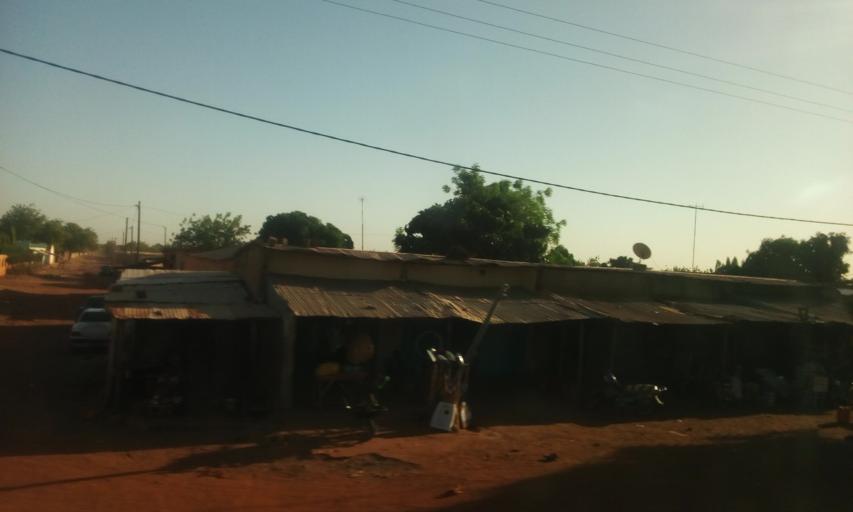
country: ML
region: Segou
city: Baroueli
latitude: 12.7844
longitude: -6.9498
